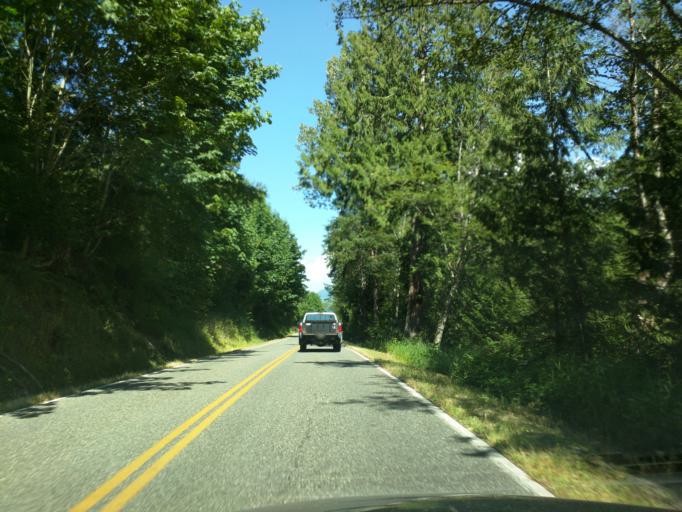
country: US
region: Washington
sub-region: Whatcom County
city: Peaceful Valley
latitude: 48.9586
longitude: -122.1977
